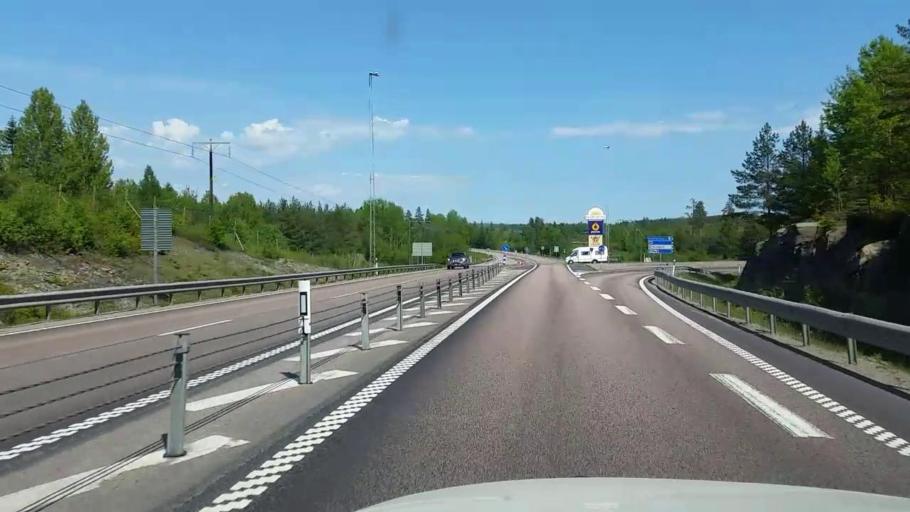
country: SE
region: Gaevleborg
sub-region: Hudiksvalls Kommun
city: Hudiksvall
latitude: 61.7416
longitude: 17.0749
